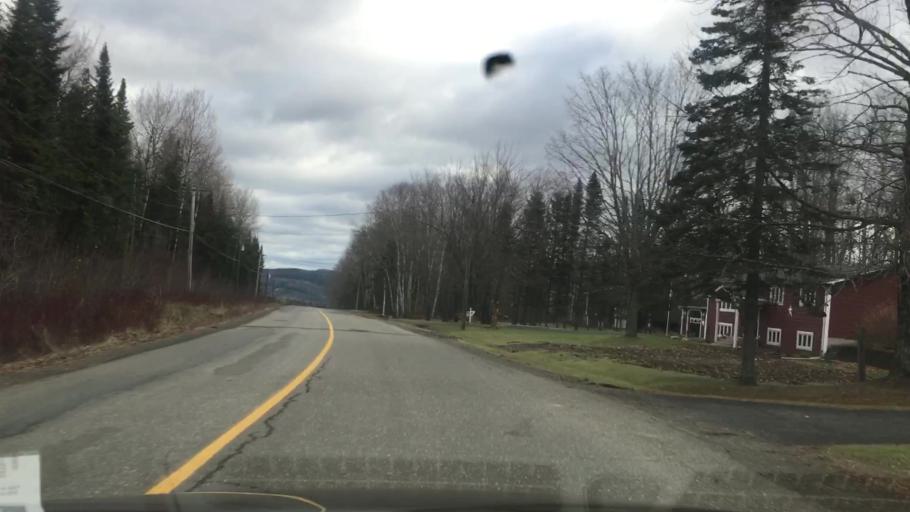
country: US
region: Maine
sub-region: Aroostook County
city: Fort Fairfield
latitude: 46.7478
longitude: -67.7460
